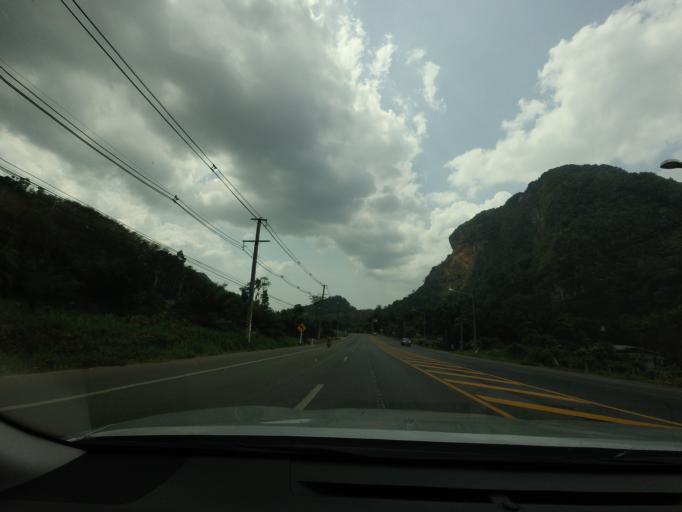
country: TH
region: Phangnga
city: Ban Ao Nang
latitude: 8.0850
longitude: 98.8056
